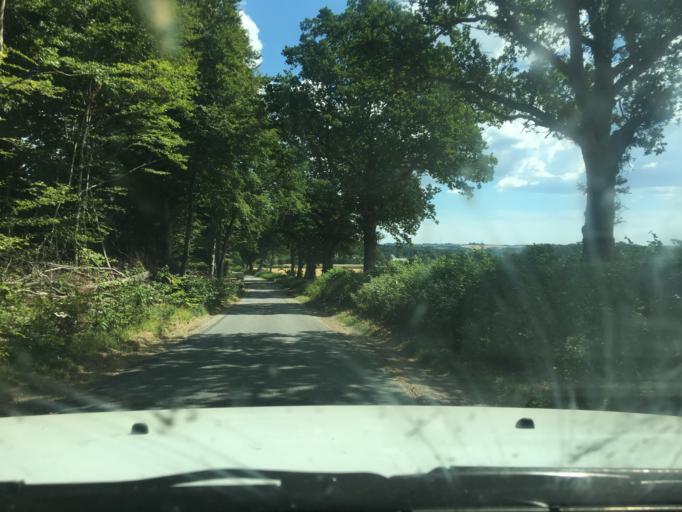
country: DK
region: Central Jutland
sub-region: Syddjurs Kommune
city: Hornslet
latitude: 56.3356
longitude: 10.3158
